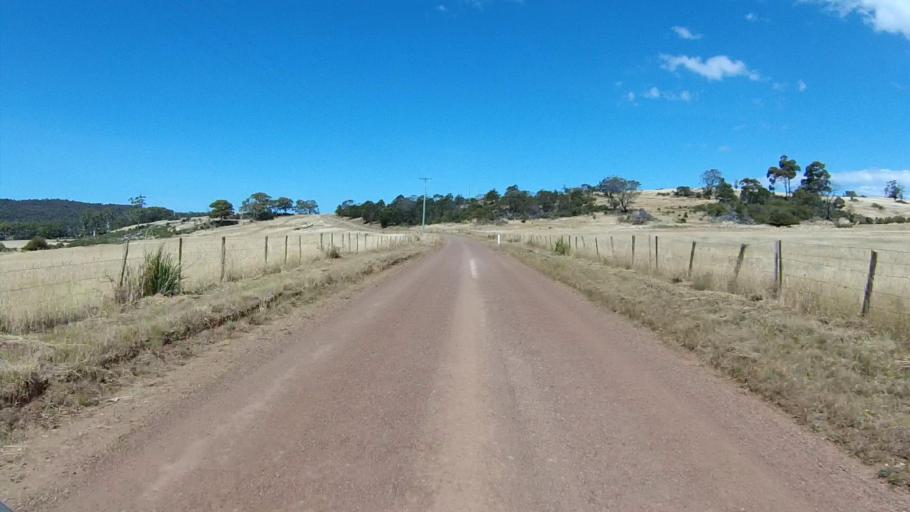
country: AU
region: Tasmania
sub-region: Break O'Day
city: St Helens
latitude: -41.9639
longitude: 148.0731
